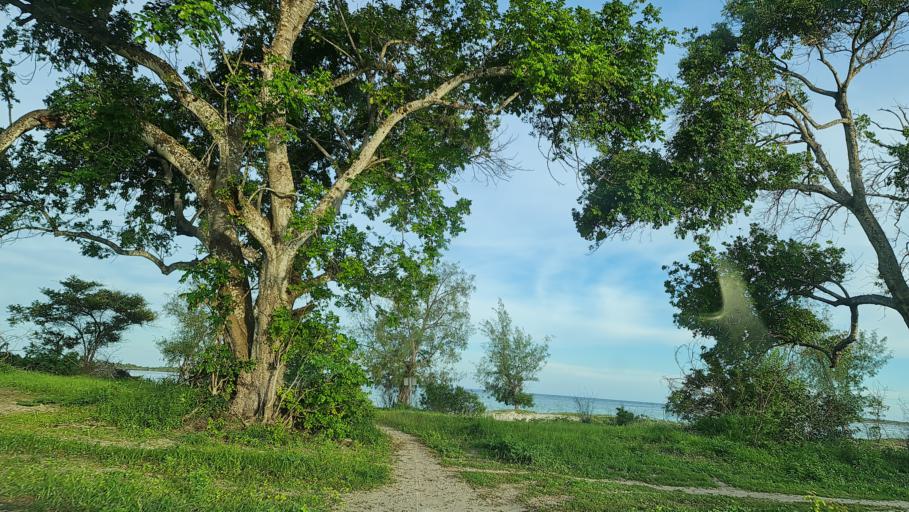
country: MZ
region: Nampula
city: Nacala
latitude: -14.7778
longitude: 40.8222
